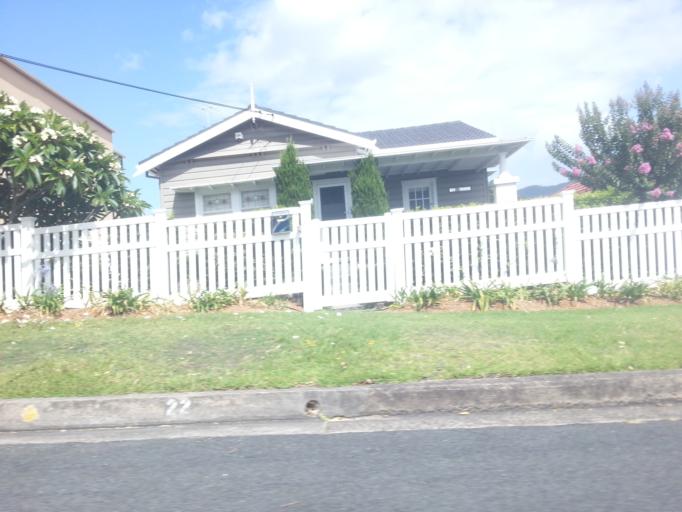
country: AU
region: New South Wales
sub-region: Wollongong
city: West Wollongong
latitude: -34.4234
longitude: 150.8735
